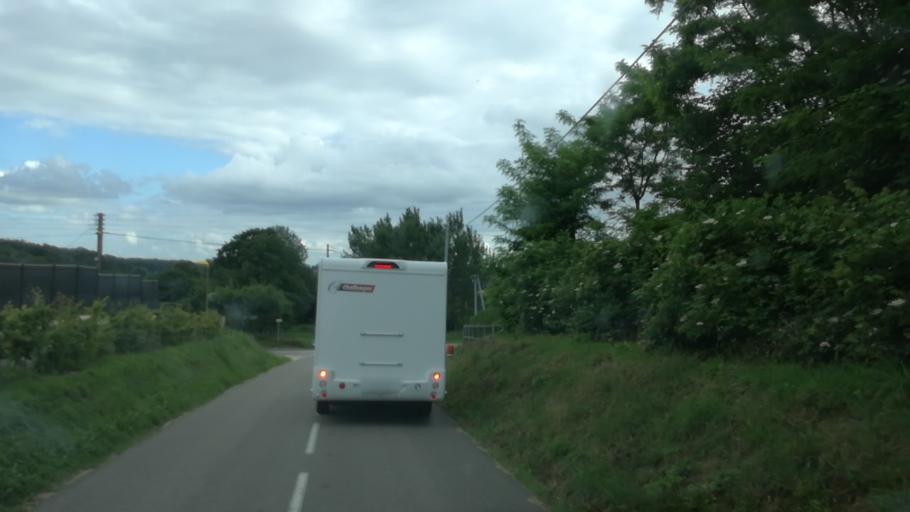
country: FR
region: Haute-Normandie
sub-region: Departement de l'Eure
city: Bourg-Achard
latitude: 49.3443
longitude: 0.8188
